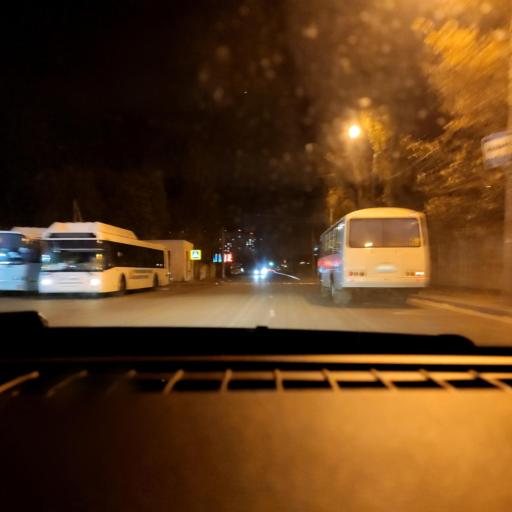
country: RU
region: Voronezj
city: Maslovka
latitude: 51.6359
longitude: 39.2838
